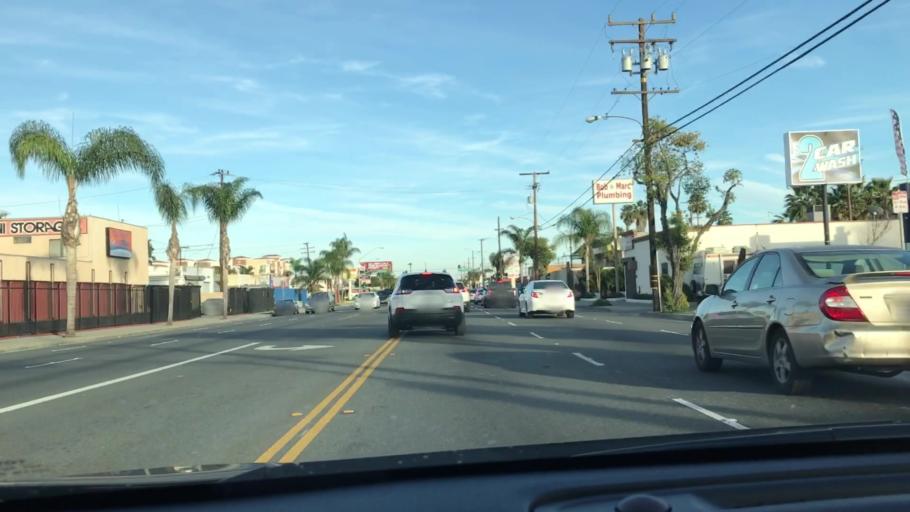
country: US
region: California
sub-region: Los Angeles County
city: Alondra Park
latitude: 33.9019
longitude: -118.3328
